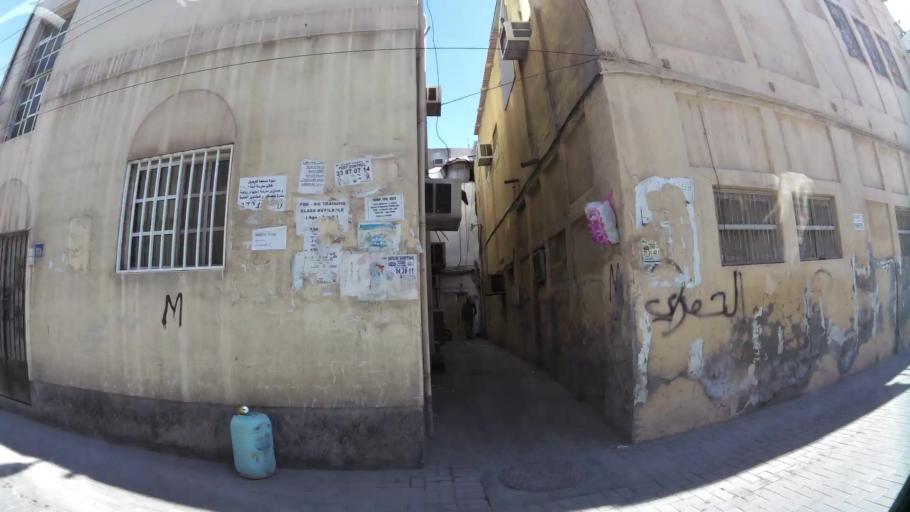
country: BH
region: Muharraq
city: Al Muharraq
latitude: 26.2477
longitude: 50.6121
